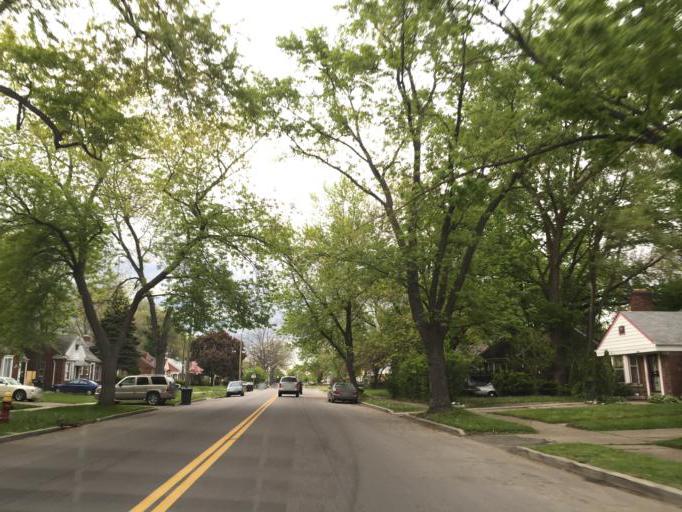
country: US
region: Michigan
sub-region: Wayne County
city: Redford
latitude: 42.4050
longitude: -83.2376
